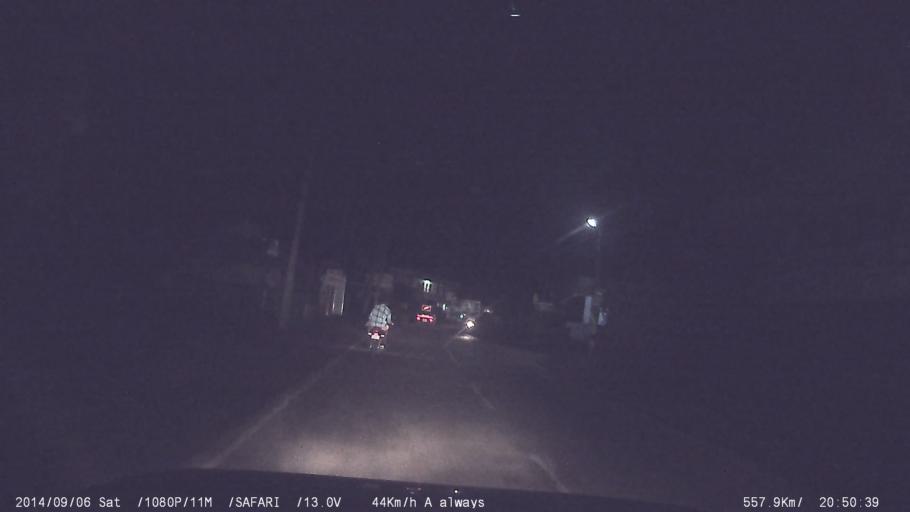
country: IN
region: Kerala
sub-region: Kottayam
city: Palackattumala
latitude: 9.7469
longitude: 76.5610
